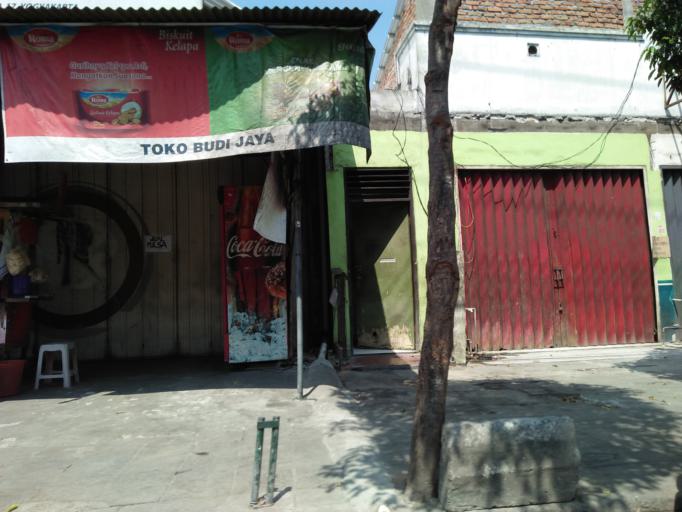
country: ID
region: Daerah Istimewa Yogyakarta
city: Kasihan
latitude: -7.8143
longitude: 110.3561
